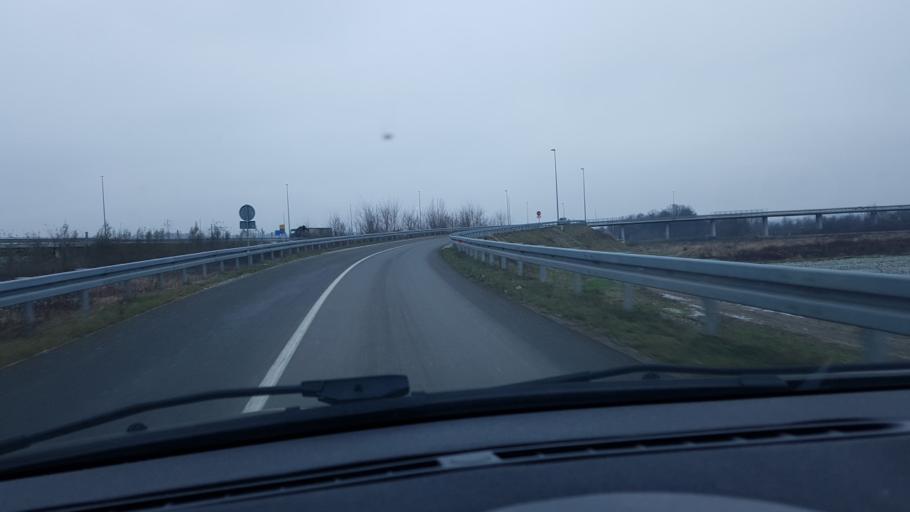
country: HR
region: Krapinsko-Zagorska
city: Zabok
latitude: 46.0168
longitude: 15.9309
